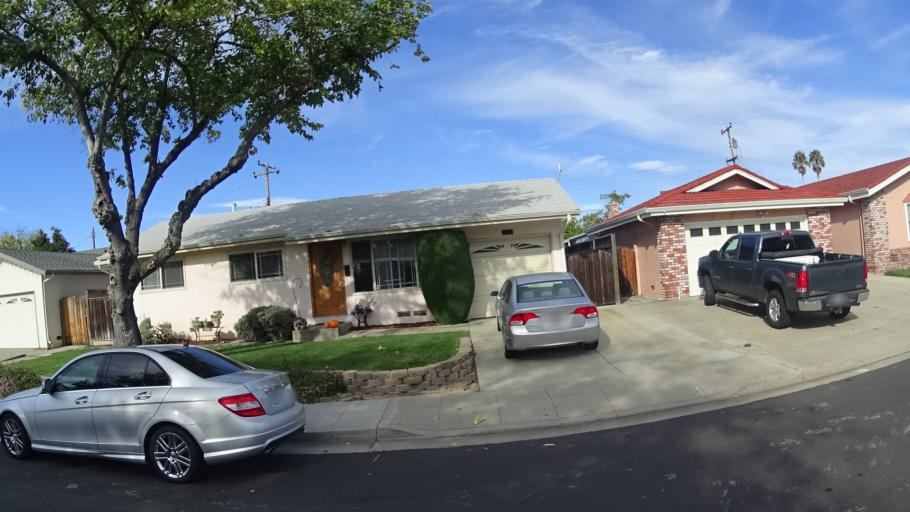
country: US
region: California
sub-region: Santa Clara County
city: Santa Clara
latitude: 37.3597
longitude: -121.9671
